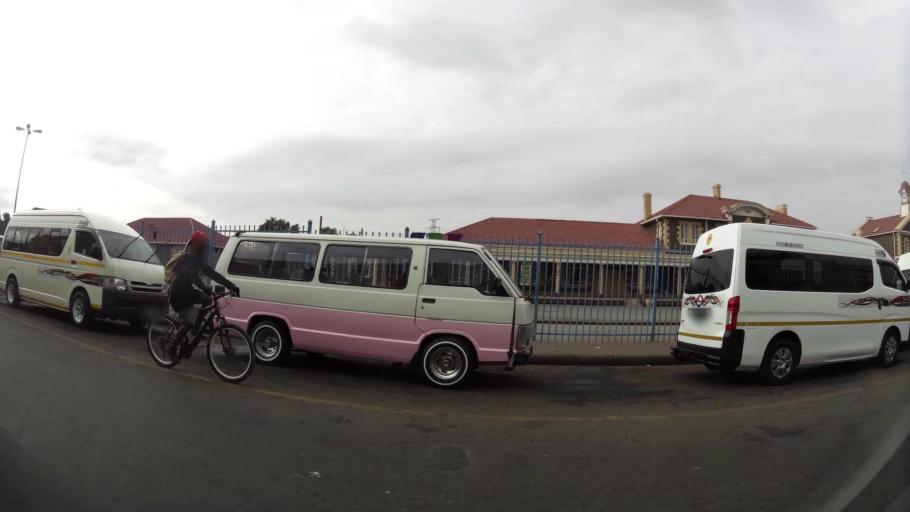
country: ZA
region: Orange Free State
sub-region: Mangaung Metropolitan Municipality
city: Bloemfontein
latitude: -29.1180
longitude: 26.2261
